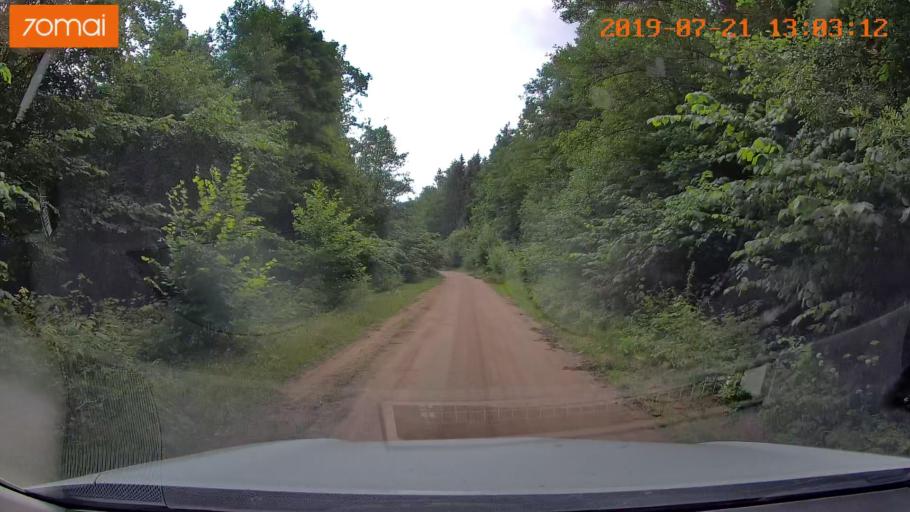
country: BY
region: Grodnenskaya
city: Lyubcha
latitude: 53.8439
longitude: 26.0240
